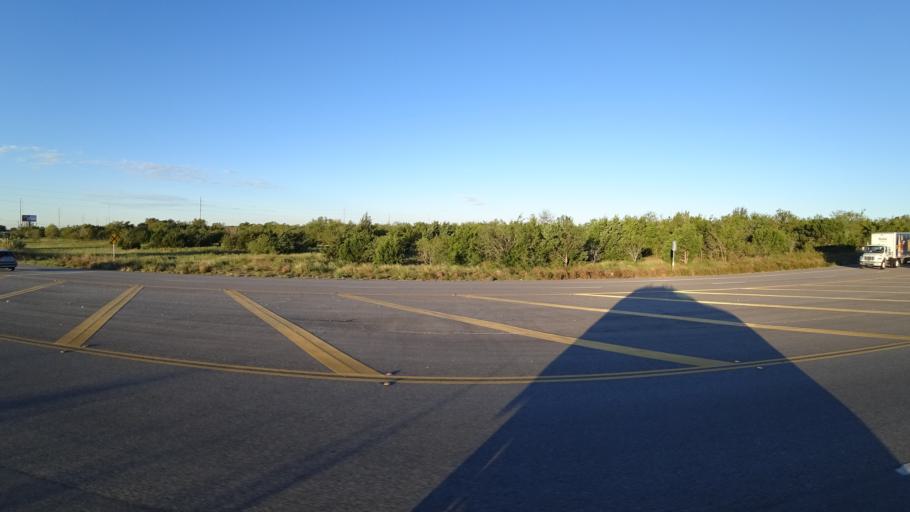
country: US
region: Texas
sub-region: Travis County
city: Manor
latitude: 30.3290
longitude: -97.6047
